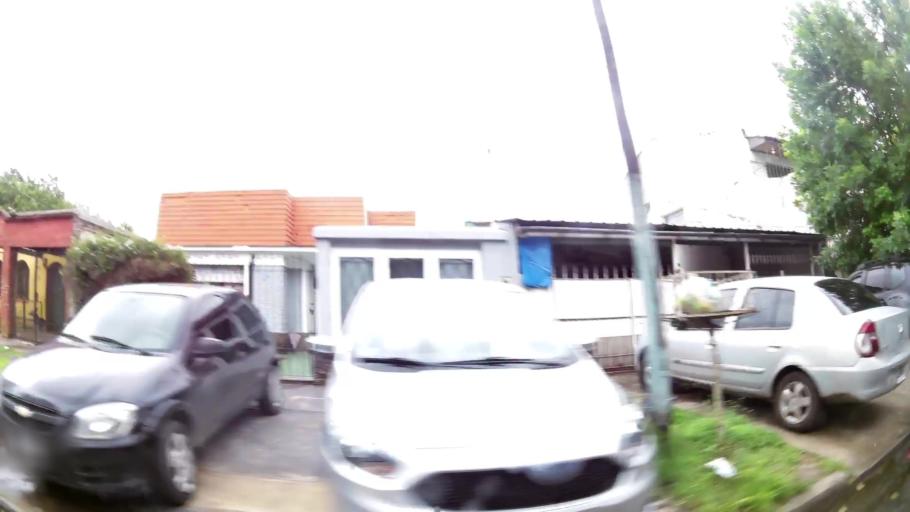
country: AR
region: Buenos Aires
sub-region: Partido de Lomas de Zamora
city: Lomas de Zamora
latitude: -34.7497
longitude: -58.3853
